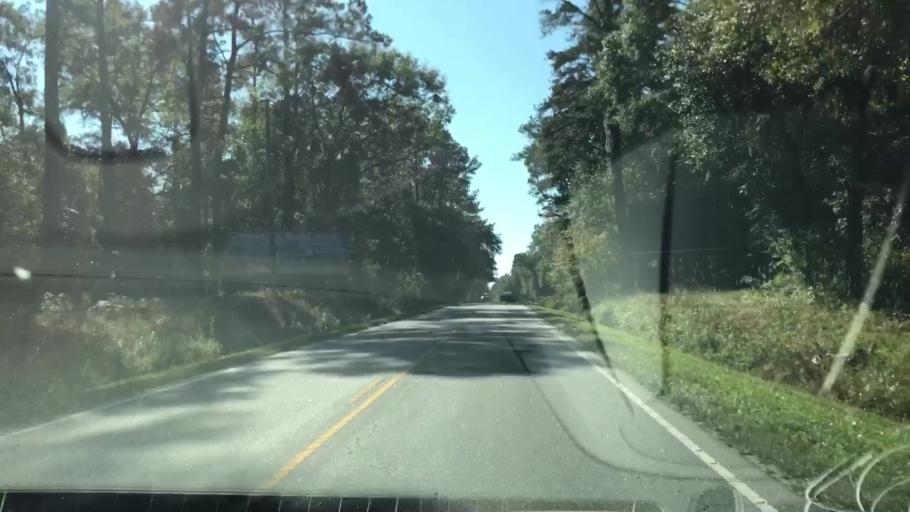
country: US
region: South Carolina
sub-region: Jasper County
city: Ridgeland
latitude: 32.3971
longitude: -80.9069
